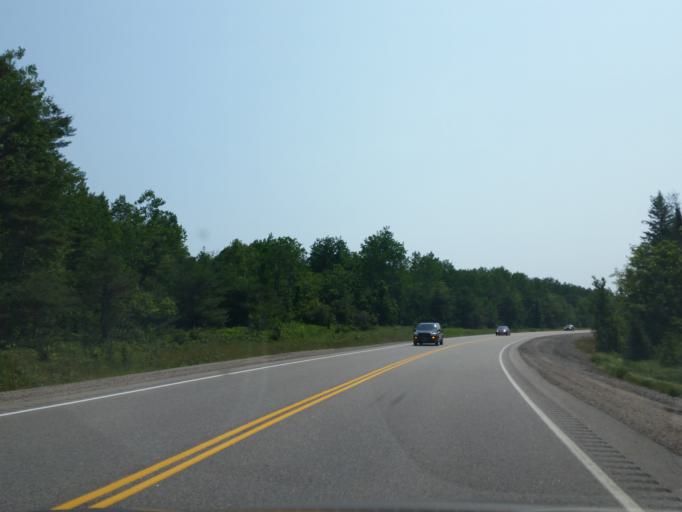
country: CA
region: Ontario
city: Mattawa
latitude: 46.2820
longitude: -78.3864
